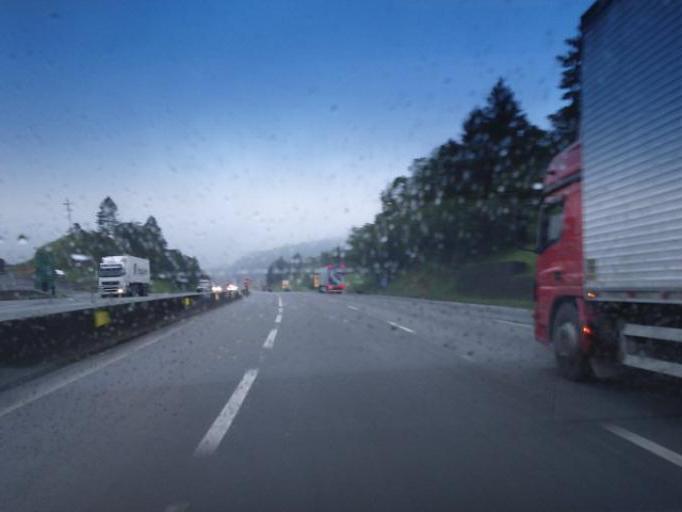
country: BR
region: Parana
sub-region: Guaratuba
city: Guaratuba
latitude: -25.8917
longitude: -48.9327
